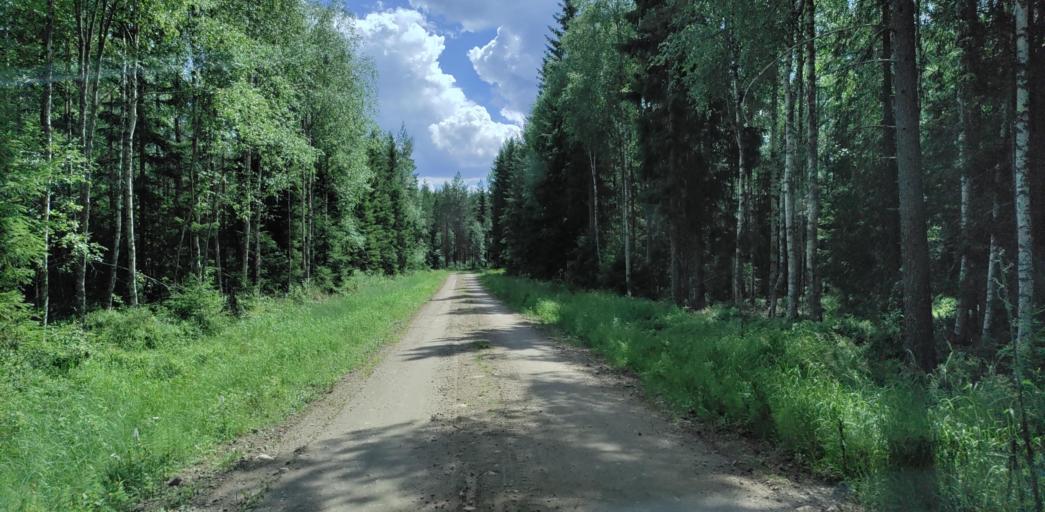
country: SE
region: Vaermland
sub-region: Hagfors Kommun
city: Ekshaerad
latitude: 60.0800
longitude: 13.3466
